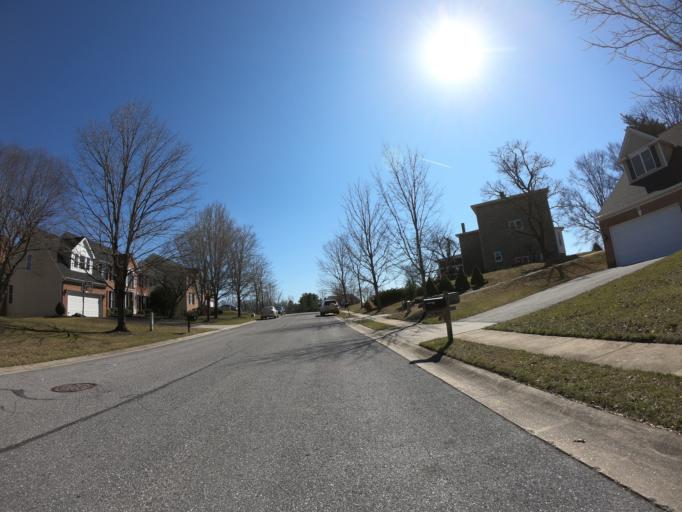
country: US
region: Maryland
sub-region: Howard County
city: Ellicott City
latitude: 39.2824
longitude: -76.7918
